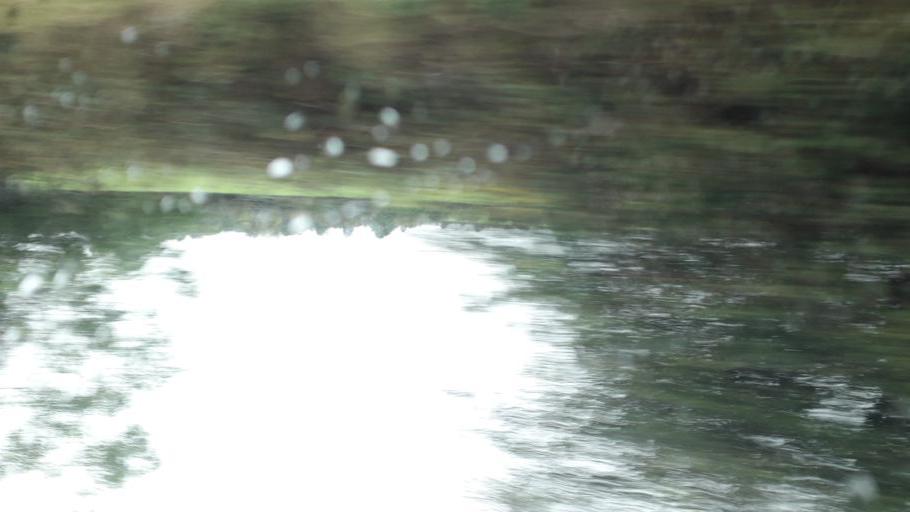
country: IE
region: Connaught
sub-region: Roscommon
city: Roscommon
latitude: 53.7863
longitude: -8.2669
